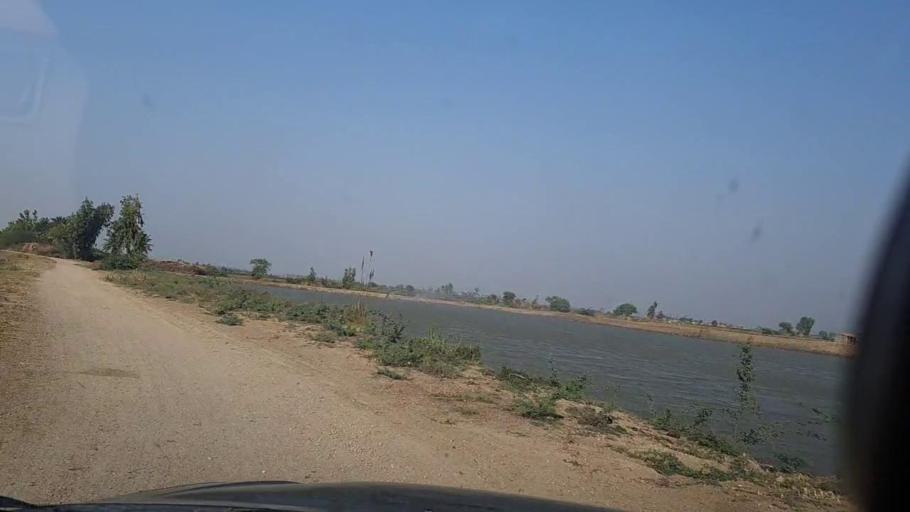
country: PK
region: Sindh
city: Thatta
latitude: 24.6085
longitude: 67.8763
